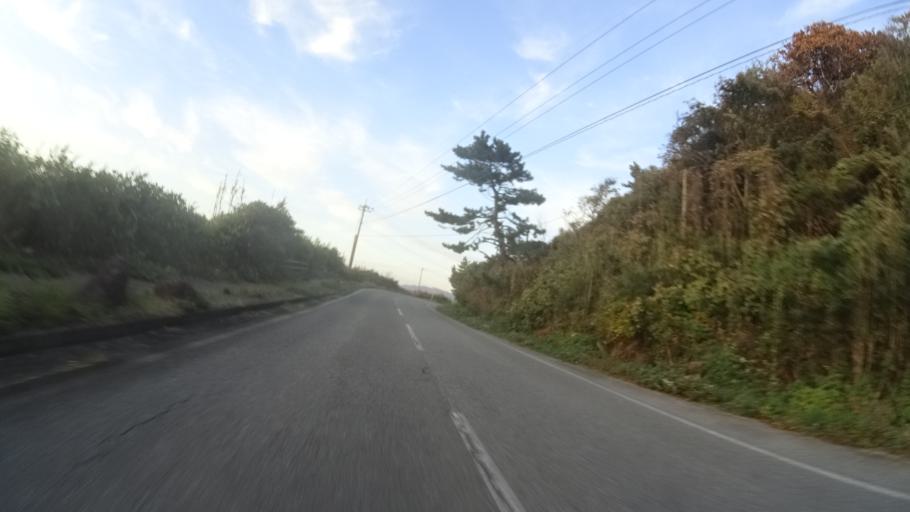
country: JP
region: Ishikawa
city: Nanao
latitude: 37.2507
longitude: 136.7167
